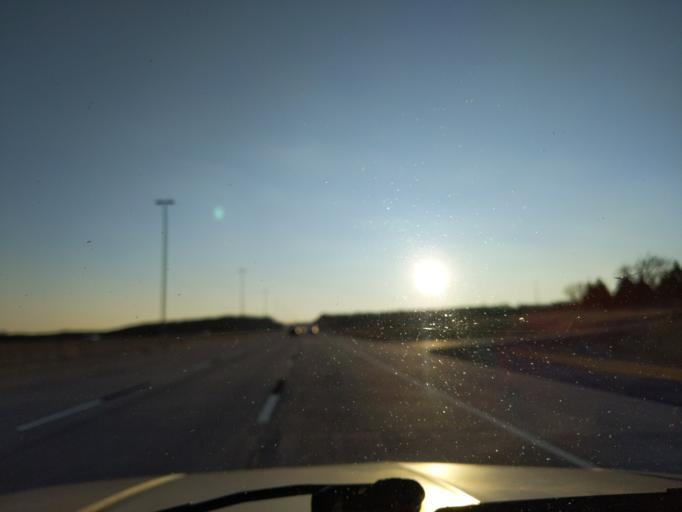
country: US
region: Oklahoma
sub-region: Creek County
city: Kellyville
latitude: 35.9128
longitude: -96.2970
